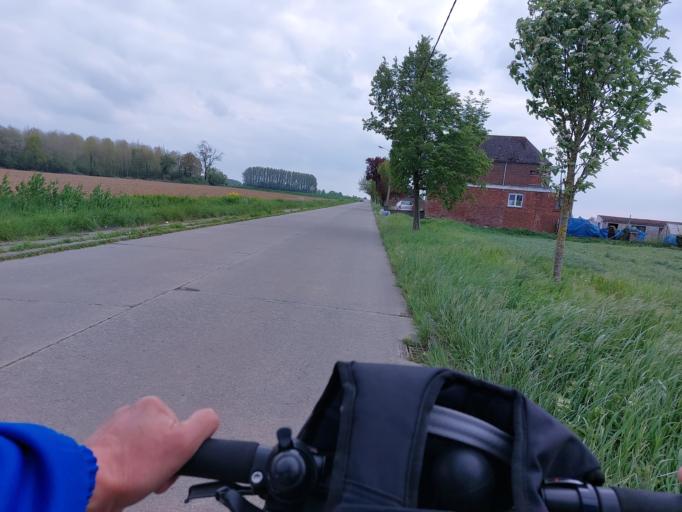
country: BE
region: Wallonia
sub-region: Province du Hainaut
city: Dour
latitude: 50.3588
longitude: 3.7372
